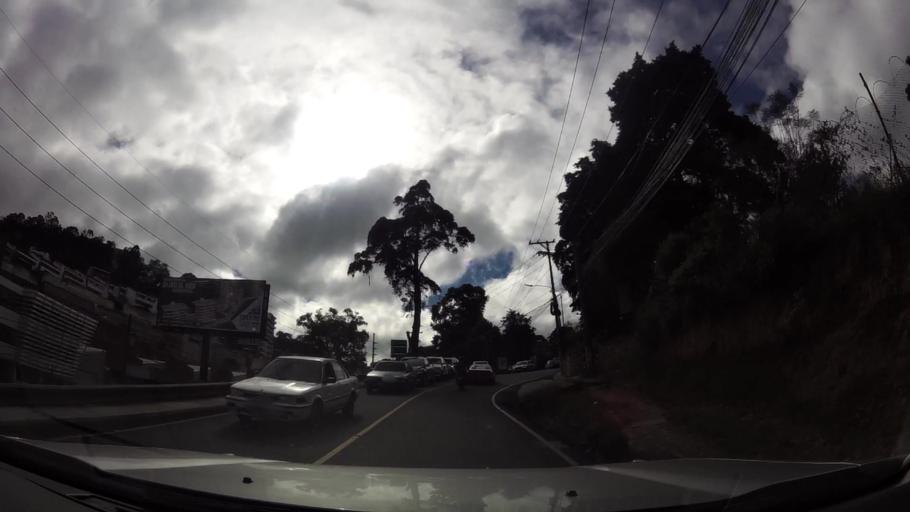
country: GT
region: Guatemala
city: Santa Catarina Pinula
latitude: 14.5730
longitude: -90.4888
